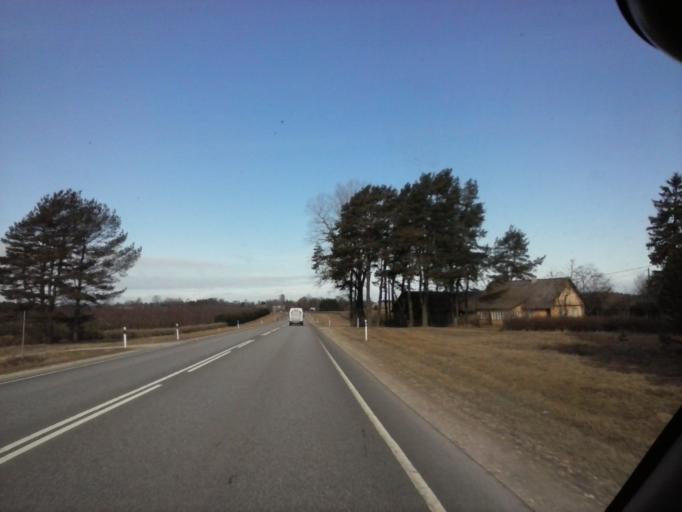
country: EE
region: Harju
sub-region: Anija vald
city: Kehra
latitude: 59.0994
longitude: 25.3730
